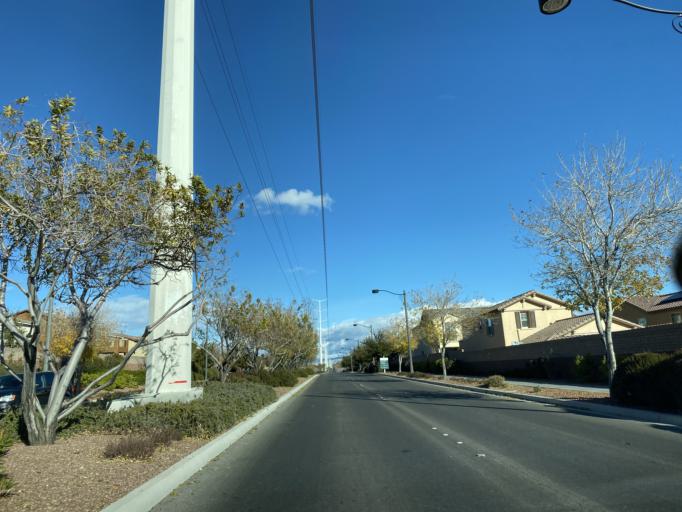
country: US
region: Nevada
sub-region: Clark County
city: Summerlin South
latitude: 36.2958
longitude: -115.3288
